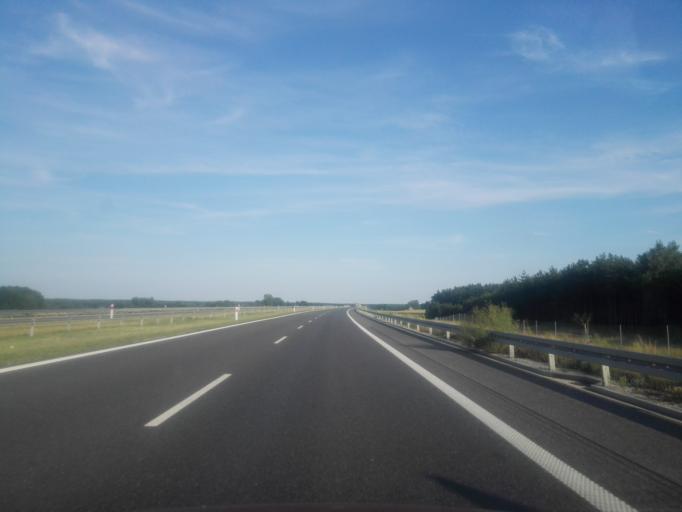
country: PL
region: Lodz Voivodeship
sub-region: Powiat wieruszowski
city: Wieruszow
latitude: 51.3309
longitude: 18.1462
